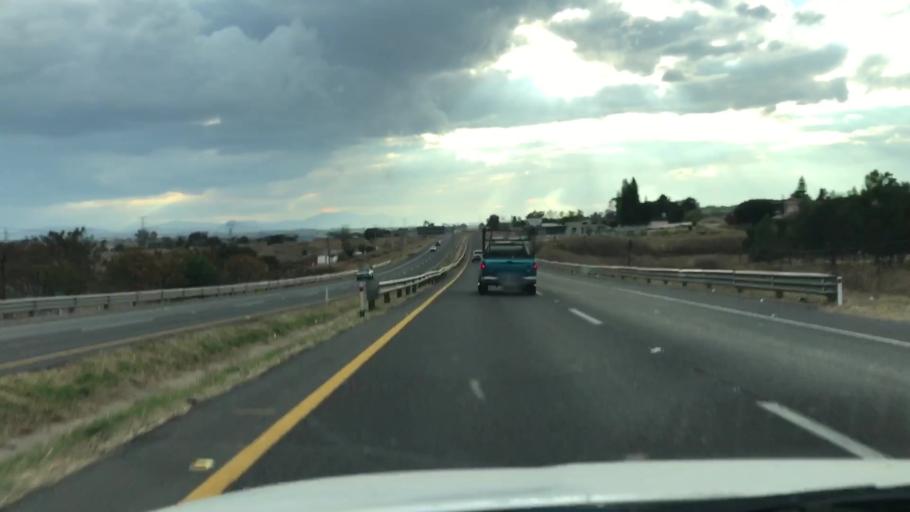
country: MX
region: Guanajuato
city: Penjamo
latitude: 20.4143
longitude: -101.7313
